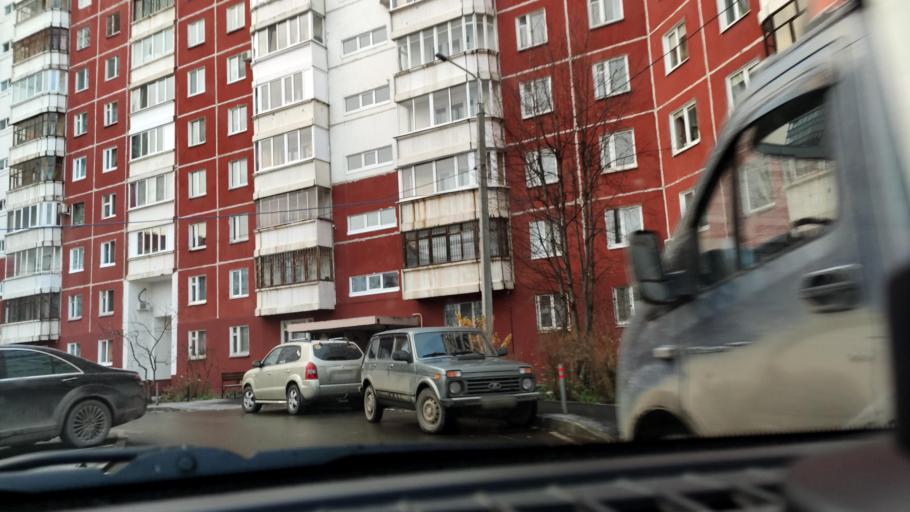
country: RU
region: Perm
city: Kondratovo
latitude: 57.9933
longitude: 56.1332
